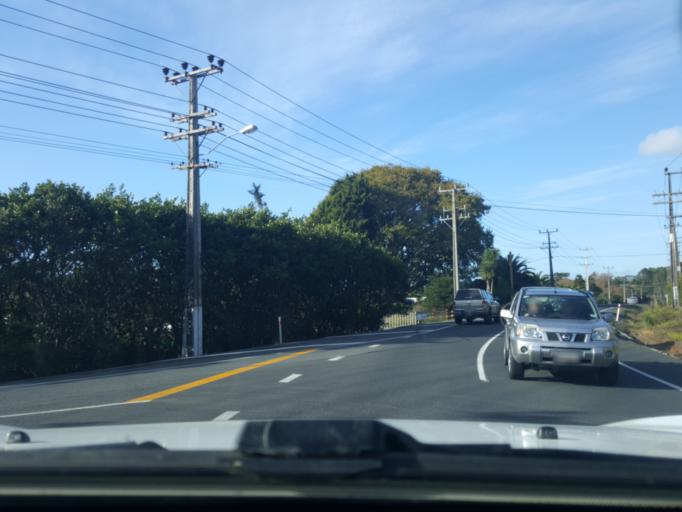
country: NZ
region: Auckland
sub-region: Auckland
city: Muriwai Beach
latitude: -36.7623
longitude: 174.5775
